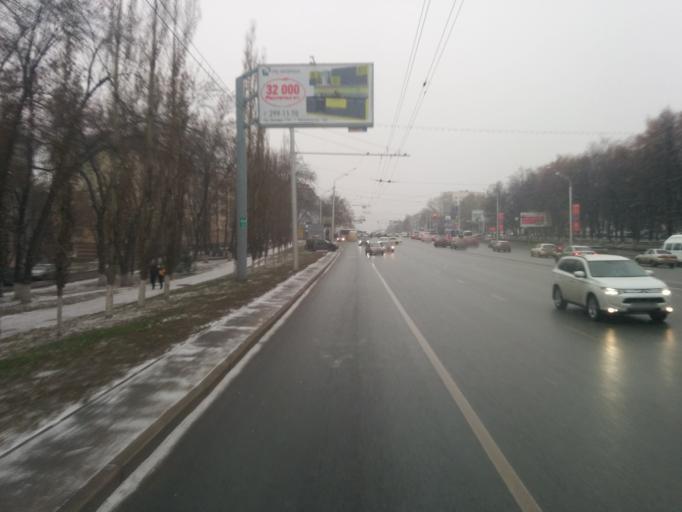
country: RU
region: Bashkortostan
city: Ufa
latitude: 54.7478
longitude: 55.9952
